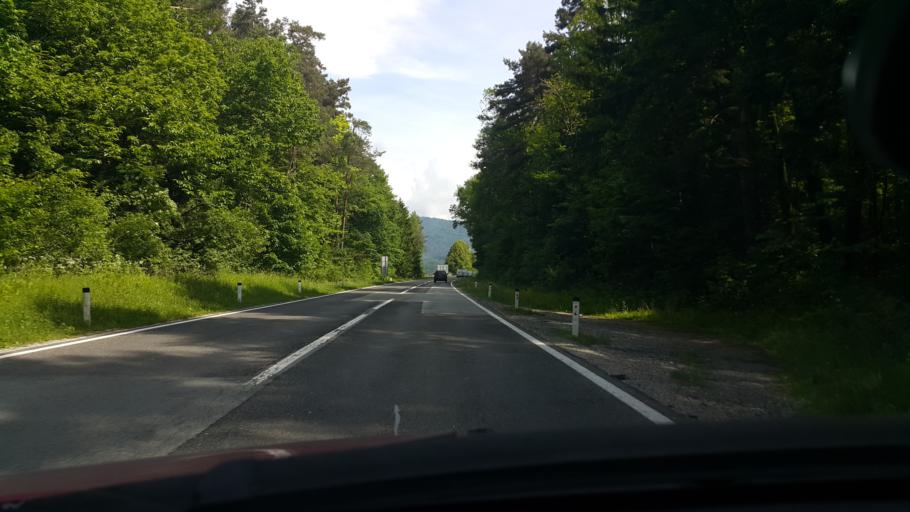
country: SI
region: Trzic
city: Bistrica pri Trzicu
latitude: 46.3199
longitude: 14.2784
